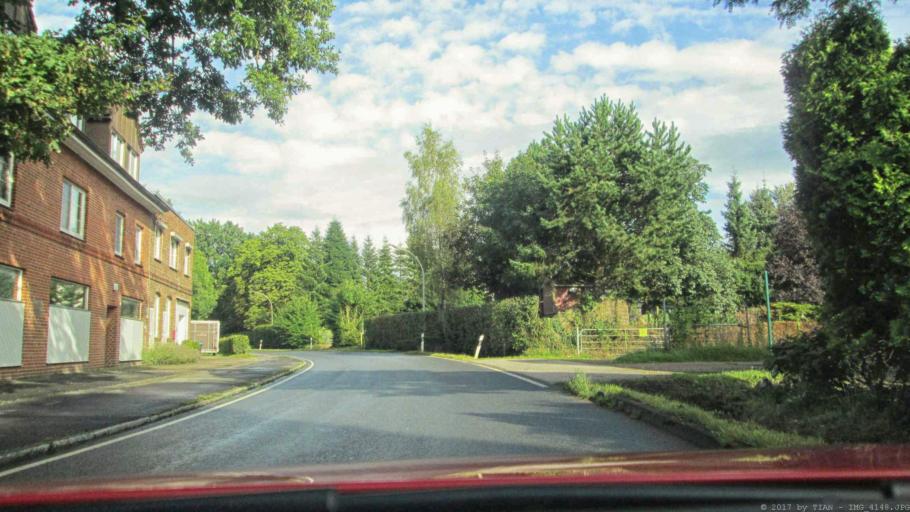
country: DE
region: Schleswig-Holstein
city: Rellingen
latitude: 53.6198
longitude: 9.8106
